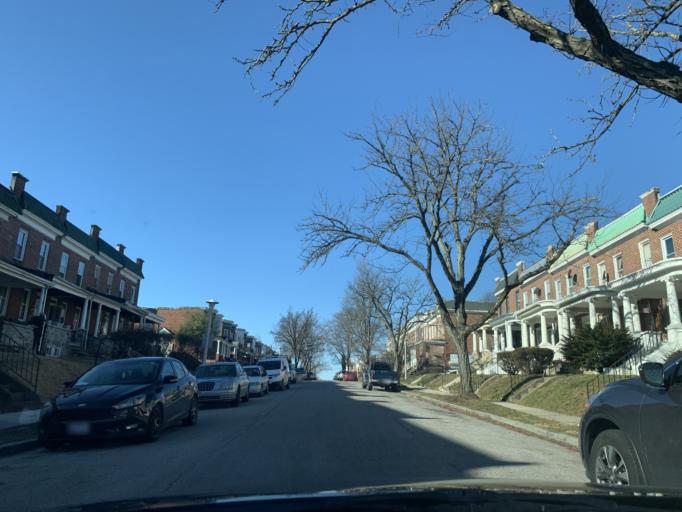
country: US
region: Maryland
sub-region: Baltimore County
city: Lochearn
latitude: 39.3163
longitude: -76.6739
